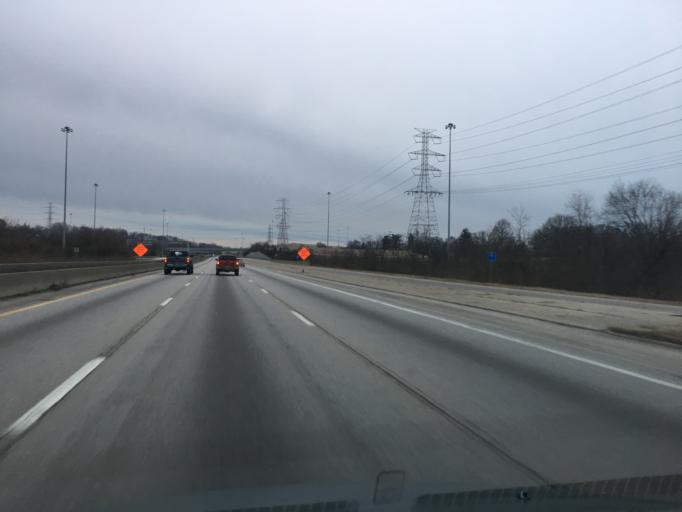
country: US
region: Ohio
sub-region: Hamilton County
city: Lockland
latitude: 39.2101
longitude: -84.4628
